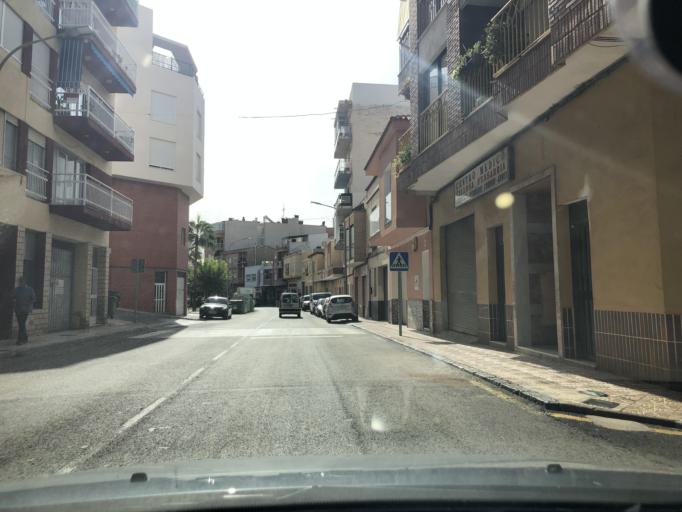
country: ES
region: Valencia
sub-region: Provincia de Alicante
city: Callosa d'En Sarria
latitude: 38.6507
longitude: -0.1255
